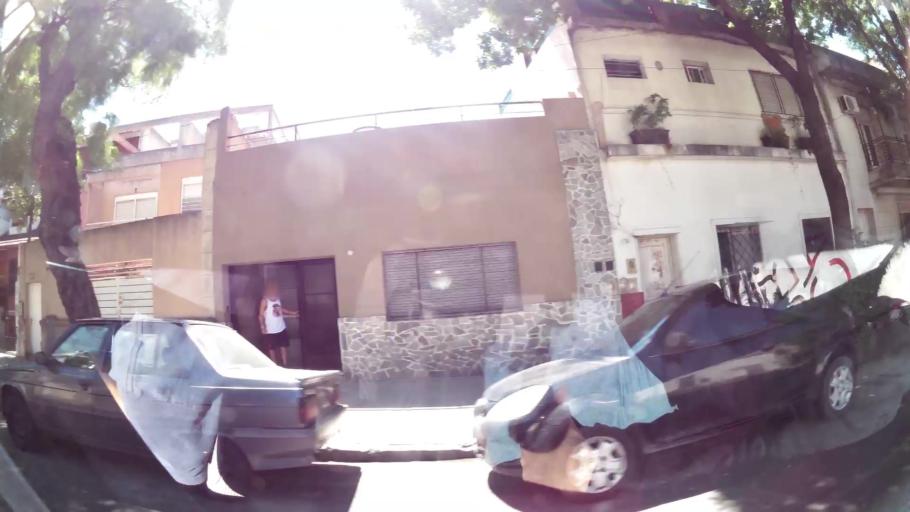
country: AR
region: Buenos Aires F.D.
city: Buenos Aires
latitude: -34.6313
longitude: -58.4130
